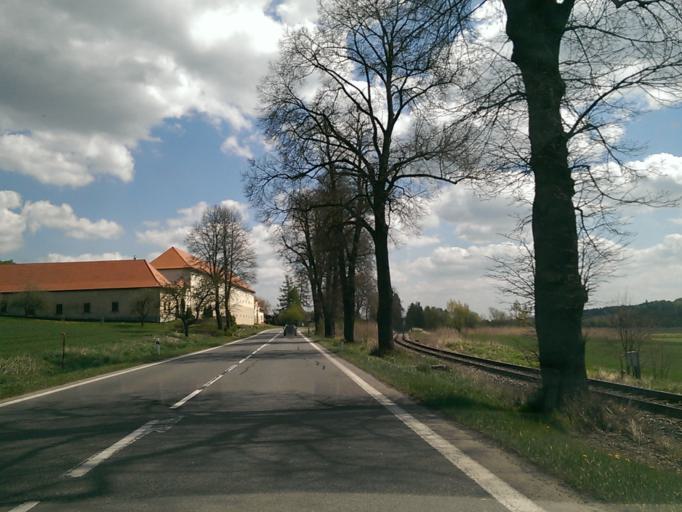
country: CZ
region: Liberecky
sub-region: Okres Semily
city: Turnov
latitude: 50.5708
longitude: 15.1779
